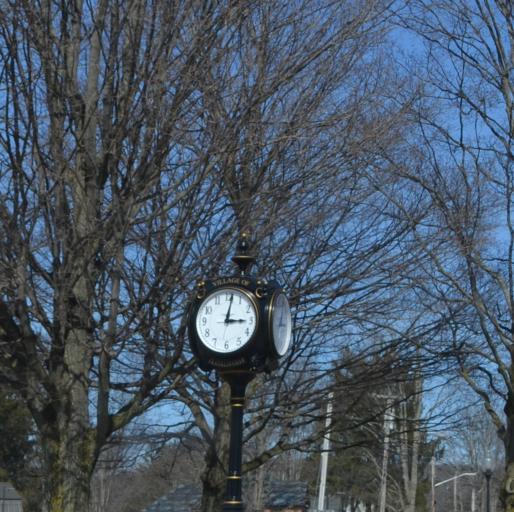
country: US
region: New York
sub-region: Cattaraugus County
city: Franklinville
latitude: 42.3370
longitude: -78.4579
